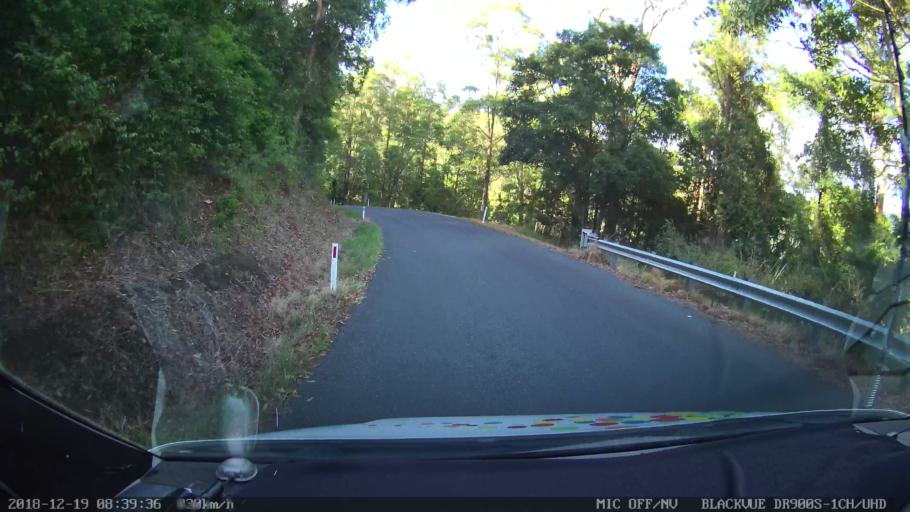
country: AU
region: New South Wales
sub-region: Kyogle
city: Kyogle
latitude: -28.3368
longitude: 152.9712
